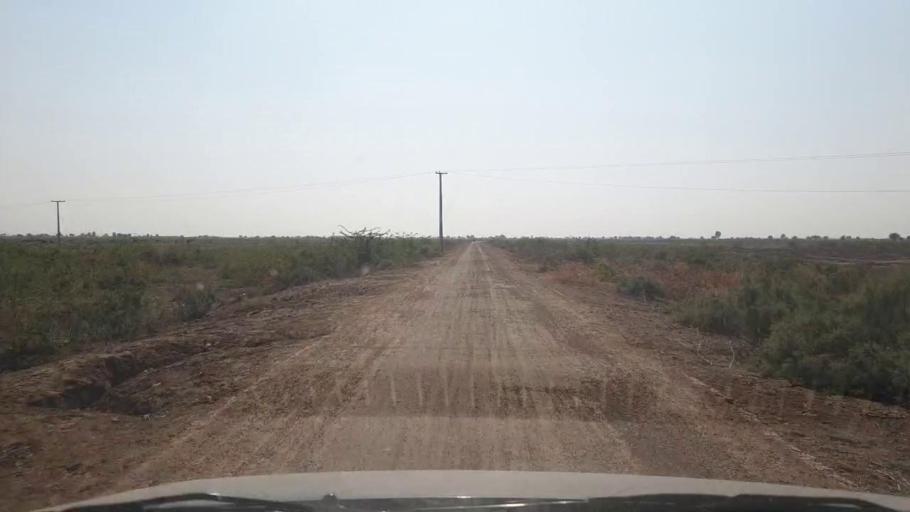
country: PK
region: Sindh
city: Samaro
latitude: 25.1918
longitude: 69.3615
